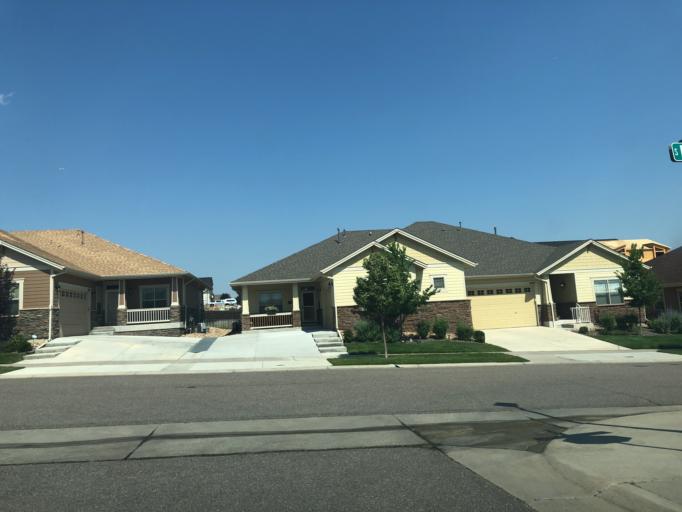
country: US
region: Colorado
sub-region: Arapahoe County
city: Dove Valley
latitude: 39.6366
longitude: -104.7612
